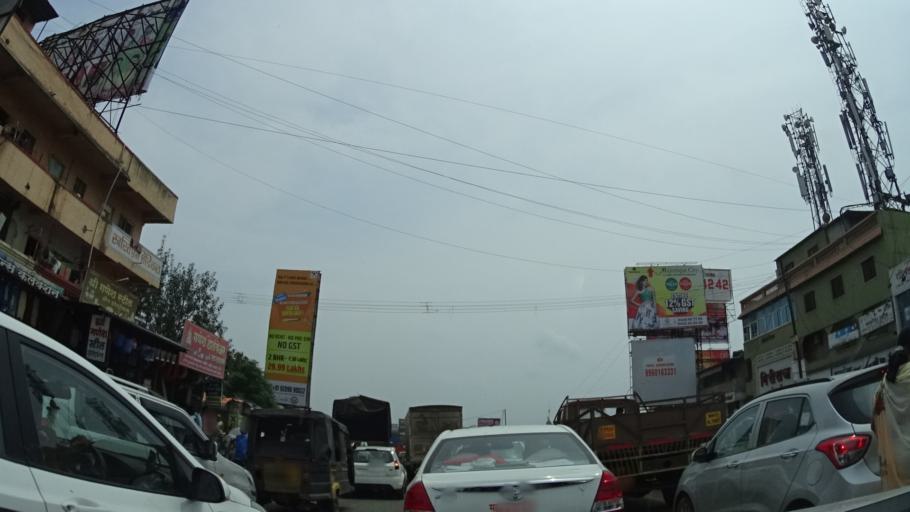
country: IN
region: Maharashtra
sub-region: Pune Division
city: Lohogaon
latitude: 18.5805
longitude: 73.9829
